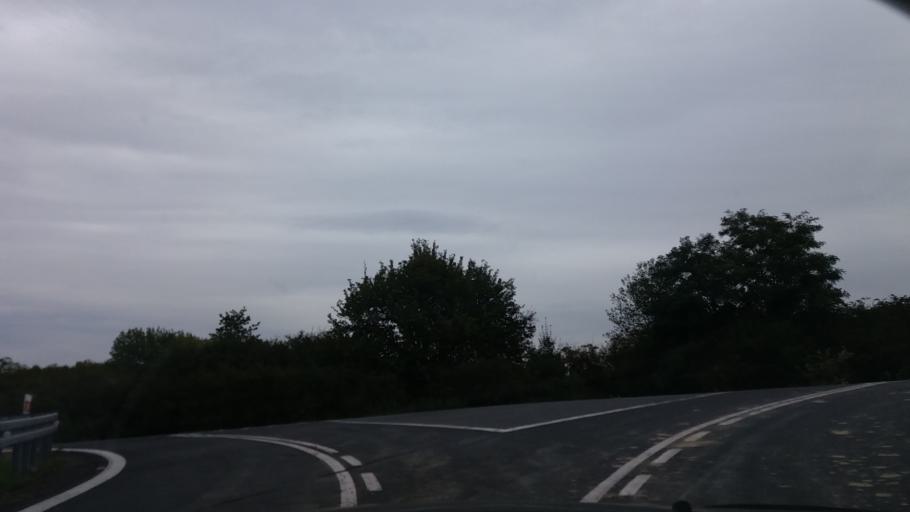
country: PL
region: Lower Silesian Voivodeship
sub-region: Powiat legnicki
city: Legnickie Pole
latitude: 51.1303
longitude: 16.3415
